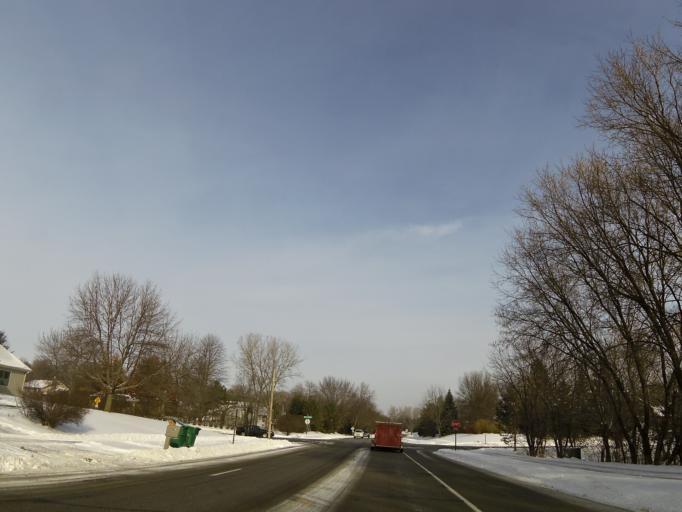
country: US
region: Minnesota
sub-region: Carver County
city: Chanhassen
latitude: 44.8731
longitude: -93.5140
